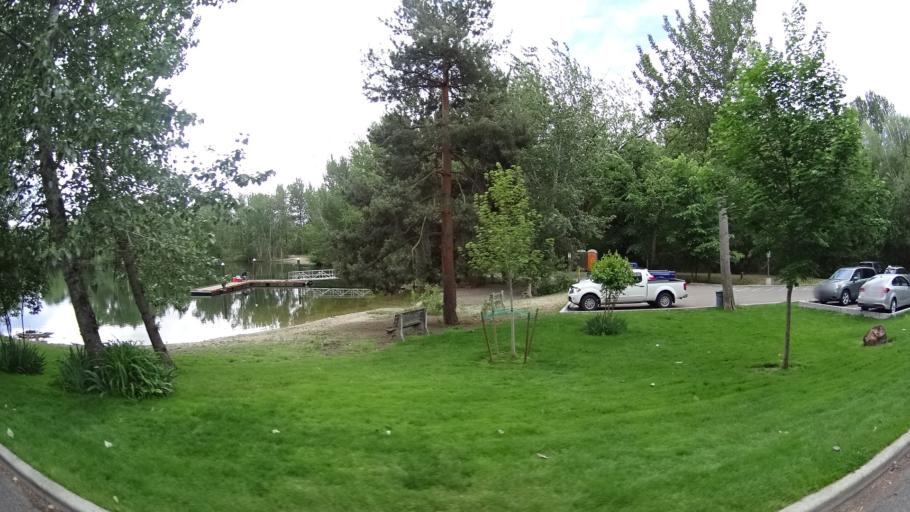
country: US
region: Idaho
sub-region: Ada County
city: Garden City
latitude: 43.6633
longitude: -116.2821
